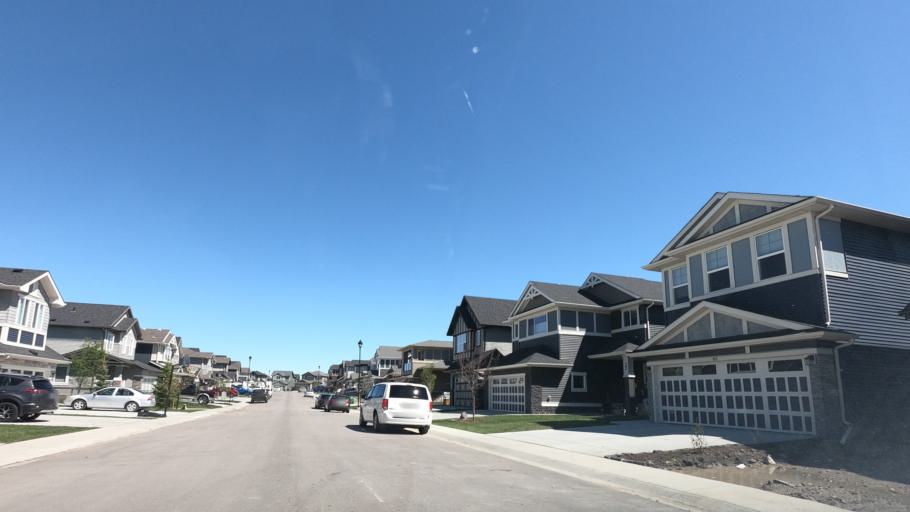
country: CA
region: Alberta
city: Airdrie
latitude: 51.2618
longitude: -113.9844
